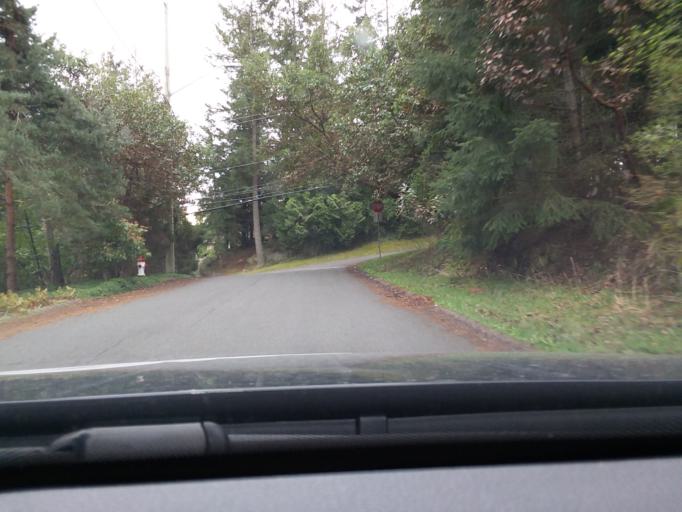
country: CA
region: British Columbia
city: North Saanich
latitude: 48.6181
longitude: -123.4254
